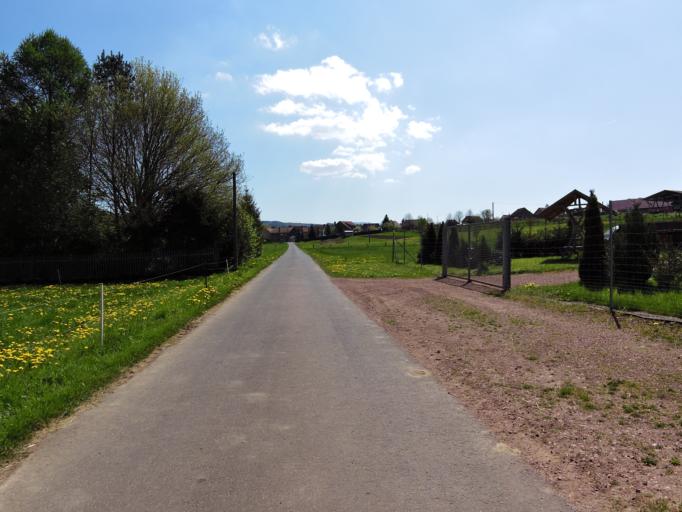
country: DE
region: Thuringia
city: Marksuhl
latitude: 50.9131
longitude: 10.1955
